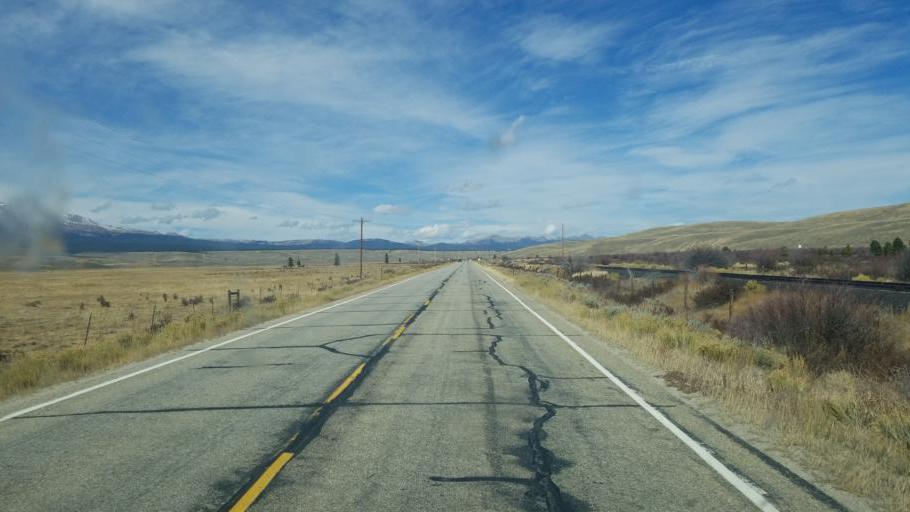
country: US
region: Colorado
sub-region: Lake County
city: Leadville
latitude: 39.1074
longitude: -106.3010
